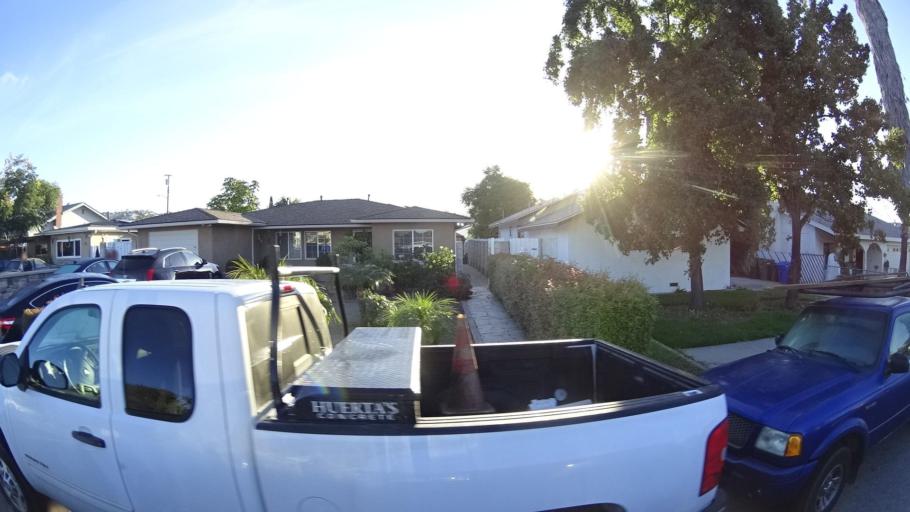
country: US
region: California
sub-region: San Diego County
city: La Presa
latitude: 32.7088
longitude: -116.9962
